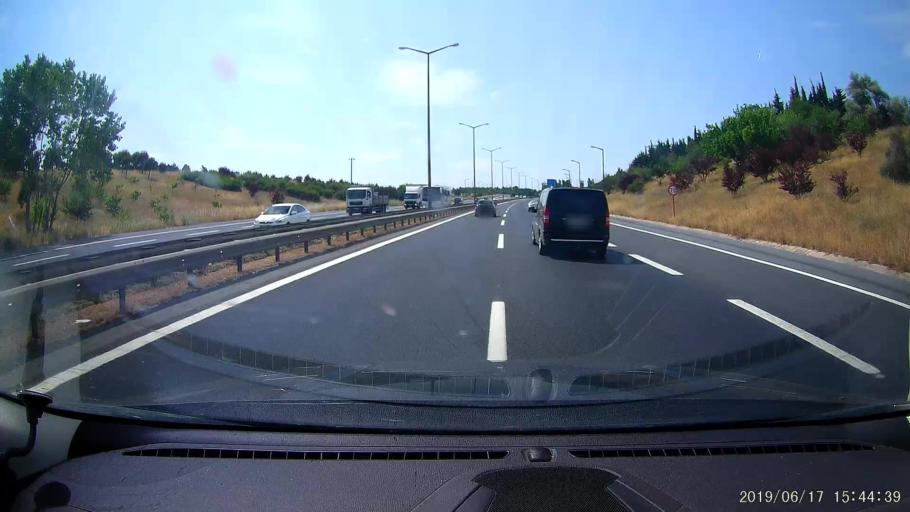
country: TR
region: Istanbul
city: Silivri
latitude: 41.1084
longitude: 28.2713
